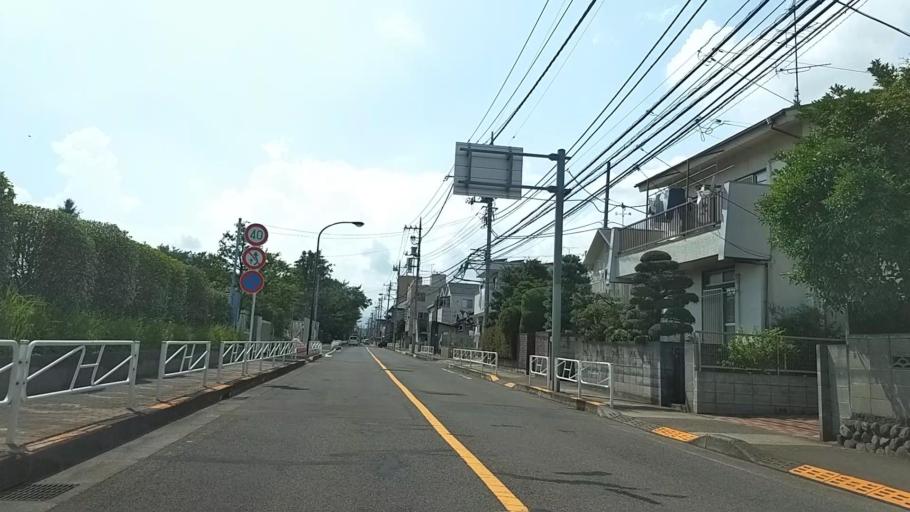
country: JP
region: Tokyo
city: Hachioji
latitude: 35.6527
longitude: 139.3266
